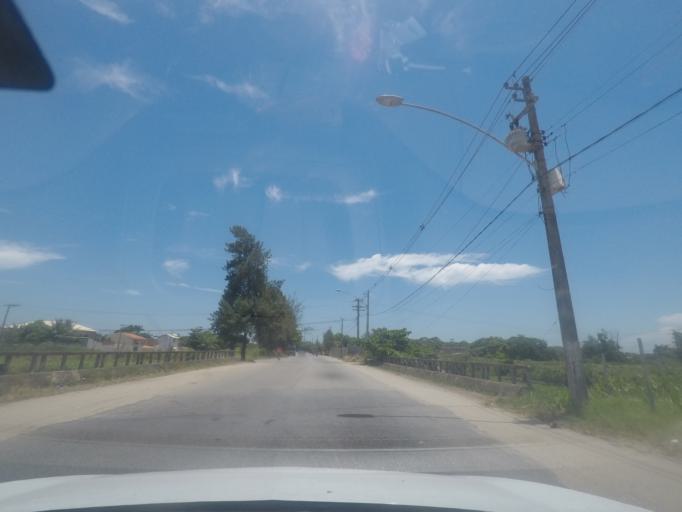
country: BR
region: Rio de Janeiro
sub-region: Itaguai
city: Itaguai
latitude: -22.9026
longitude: -43.6913
